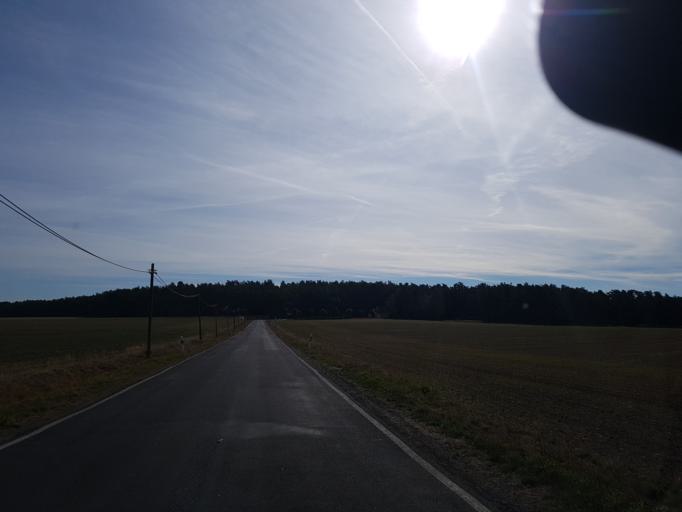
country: DE
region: Brandenburg
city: Schlieben
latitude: 51.6989
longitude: 13.4182
